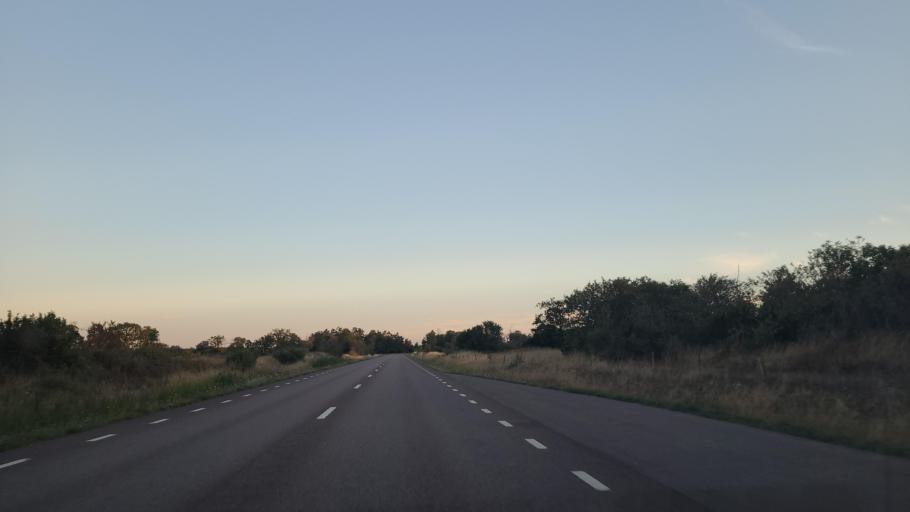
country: SE
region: Kalmar
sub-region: Borgholms Kommun
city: Borgholm
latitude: 57.0889
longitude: 16.9234
